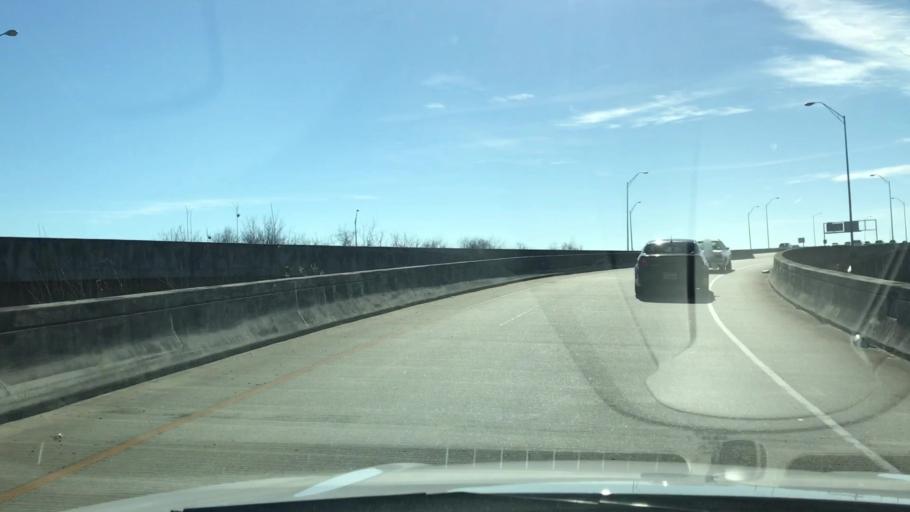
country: US
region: South Carolina
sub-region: Charleston County
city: Charleston
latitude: 32.7750
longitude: -79.9585
